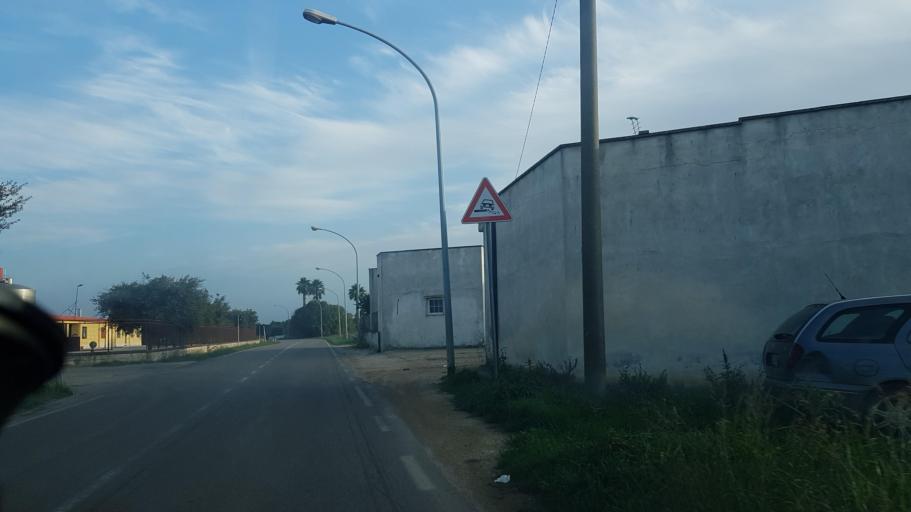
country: IT
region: Apulia
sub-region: Provincia di Brindisi
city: Mesagne
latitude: 40.5564
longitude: 17.8233
